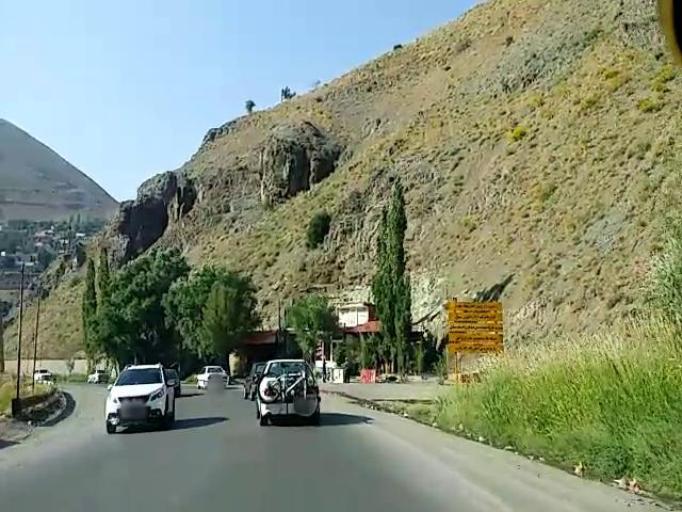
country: IR
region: Tehran
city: Tajrish
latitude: 36.0999
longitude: 51.3157
